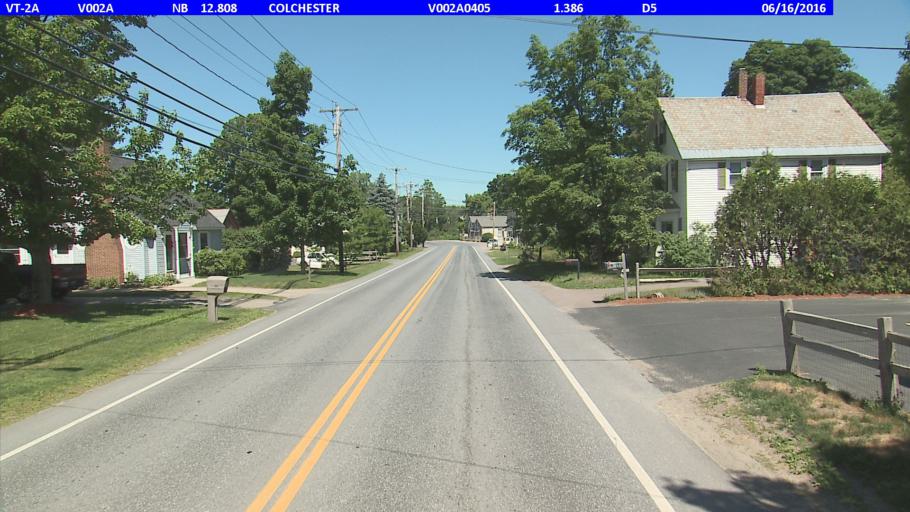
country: US
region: Vermont
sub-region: Chittenden County
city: Colchester
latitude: 44.5427
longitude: -73.1472
